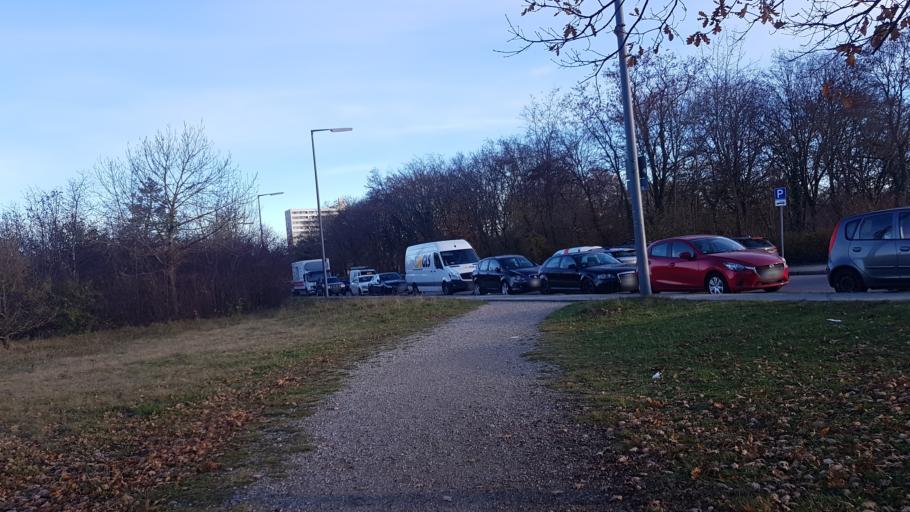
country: DE
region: Bavaria
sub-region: Upper Bavaria
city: Oberschleissheim
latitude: 48.2090
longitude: 11.5466
